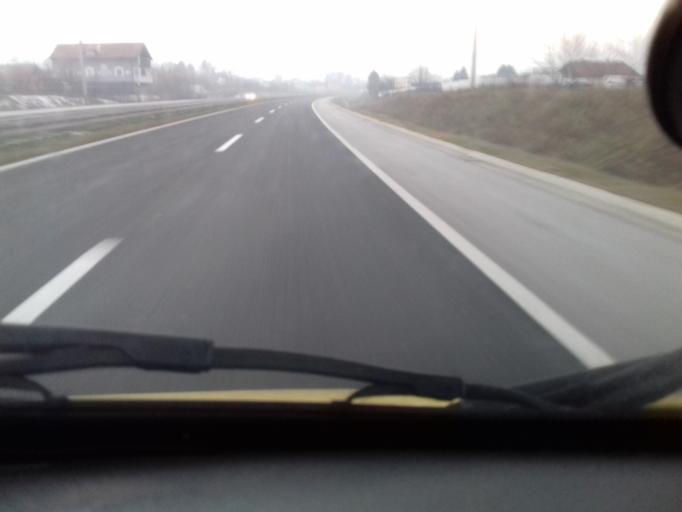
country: BA
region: Federation of Bosnia and Herzegovina
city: Gornje Mostre
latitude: 44.0062
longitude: 18.1516
